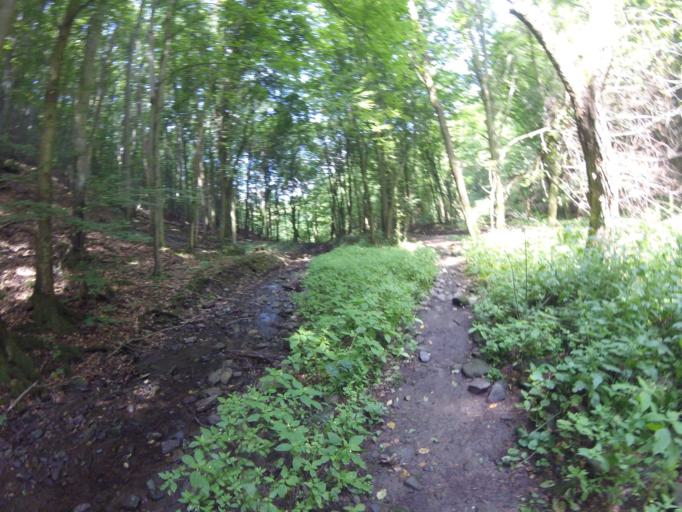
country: SK
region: Nitriansky
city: Sahy
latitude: 47.9666
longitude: 18.8969
